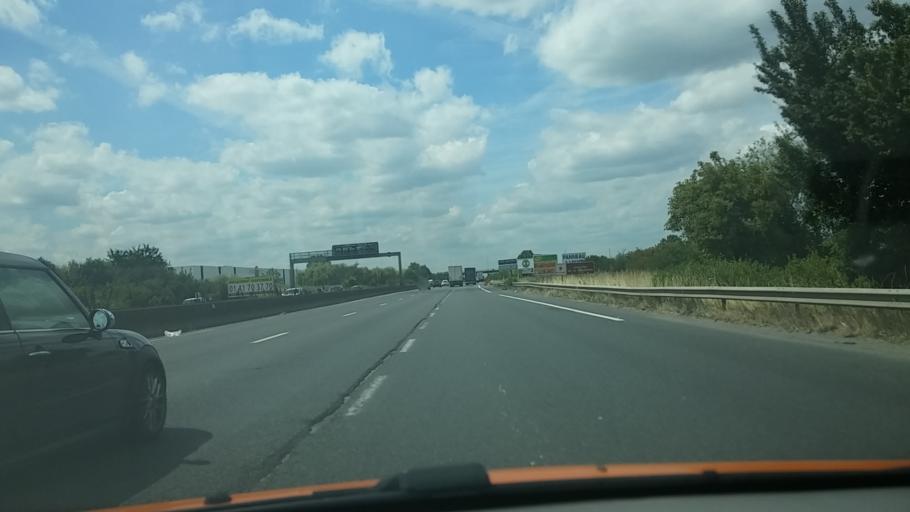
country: FR
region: Ile-de-France
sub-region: Departement de Seine-Saint-Denis
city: Tremblay-en-France
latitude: 48.9711
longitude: 2.5722
